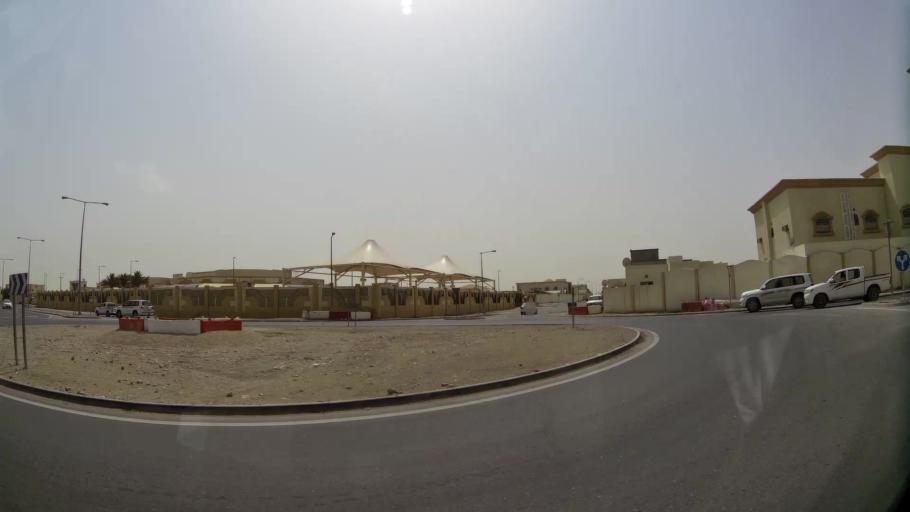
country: QA
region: Baladiyat ar Rayyan
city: Ar Rayyan
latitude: 25.2346
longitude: 51.3828
